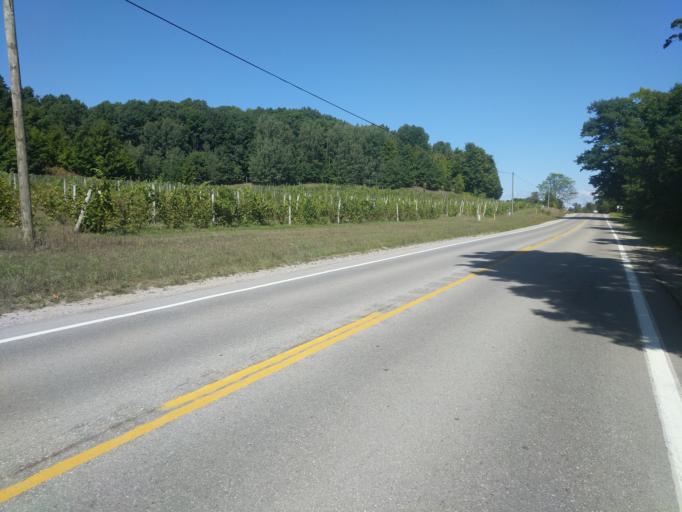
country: US
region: Michigan
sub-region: Leelanau County
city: Leland
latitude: 45.0064
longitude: -85.6244
